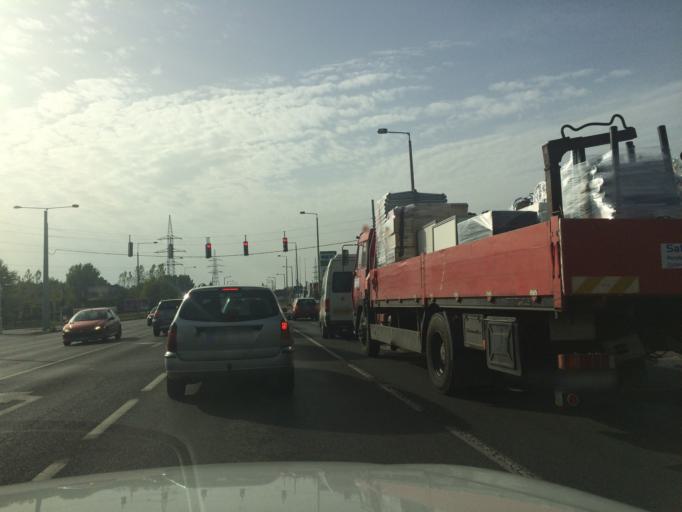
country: HU
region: Szabolcs-Szatmar-Bereg
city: Nyiregyhaza
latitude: 47.9370
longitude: 21.7188
